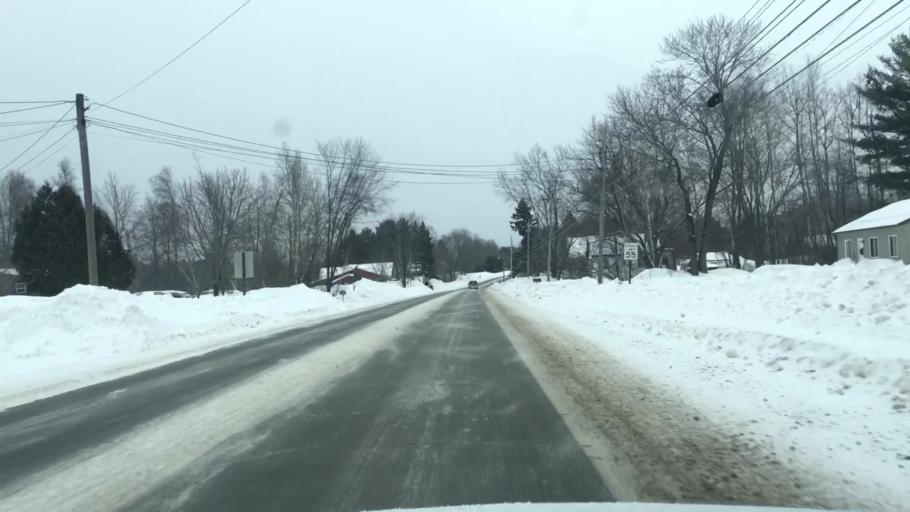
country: US
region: Maine
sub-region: Penobscot County
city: Lincoln
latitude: 45.3992
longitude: -68.4914
